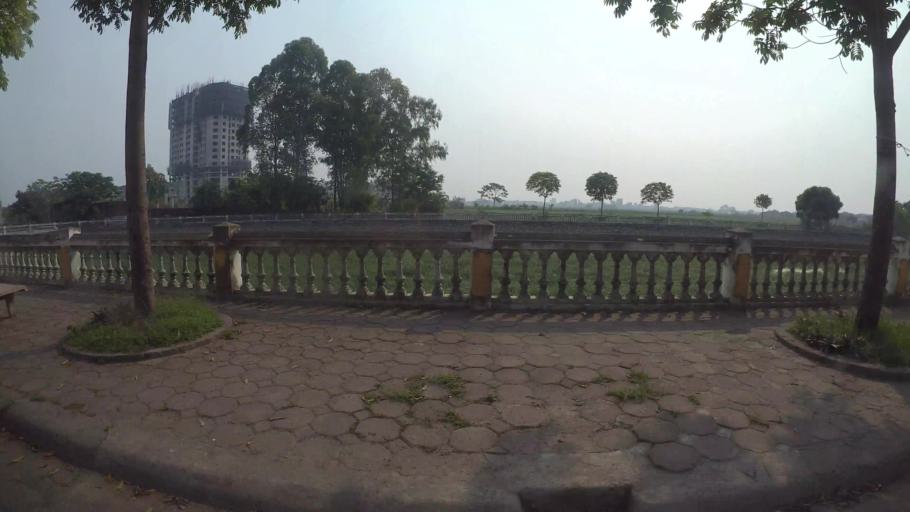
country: VN
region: Ha Noi
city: Ha Dong
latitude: 20.9933
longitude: 105.7539
